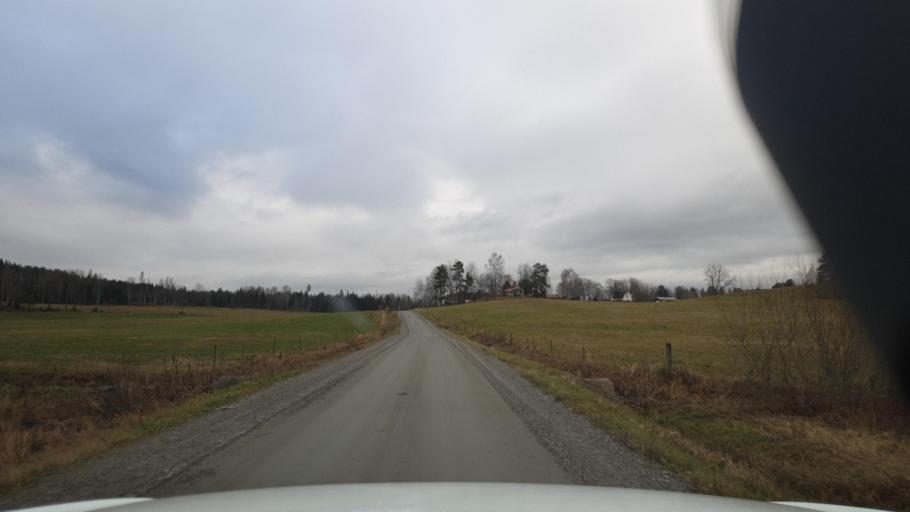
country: SE
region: Vaermland
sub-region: Karlstads Kommun
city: Edsvalla
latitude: 59.5511
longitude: 13.0106
